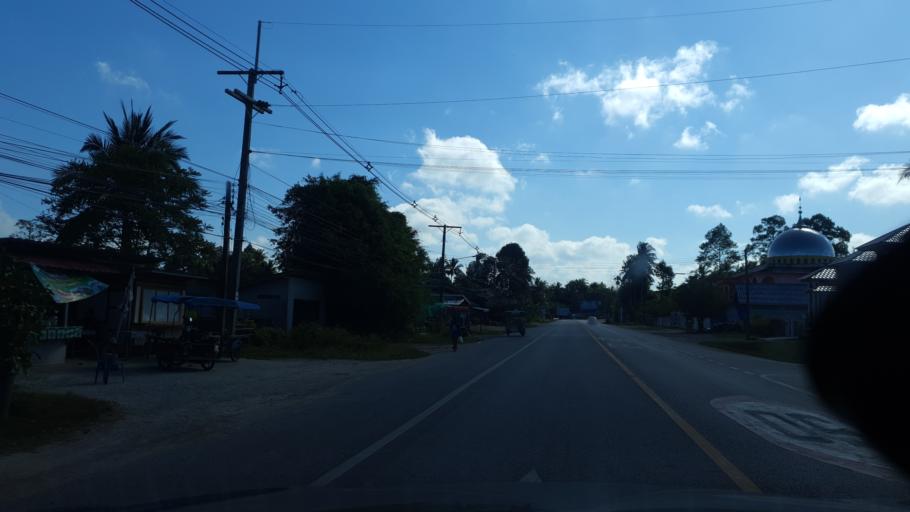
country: TH
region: Krabi
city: Krabi
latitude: 8.0262
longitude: 98.8802
